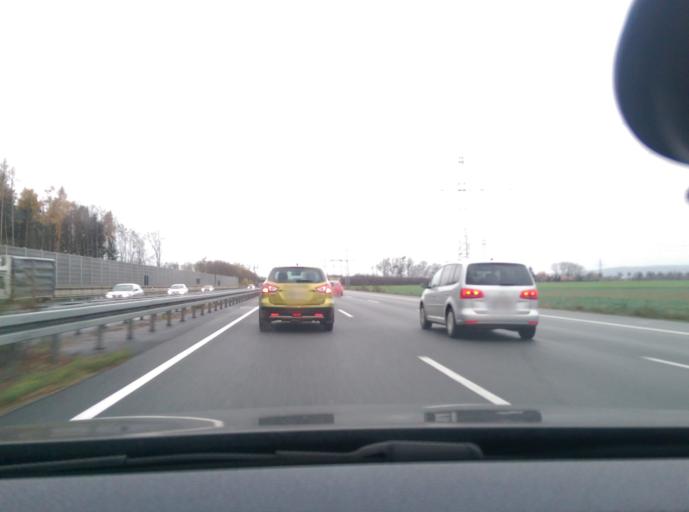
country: DE
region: Lower Saxony
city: Rosdorf
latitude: 51.4980
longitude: 9.8780
